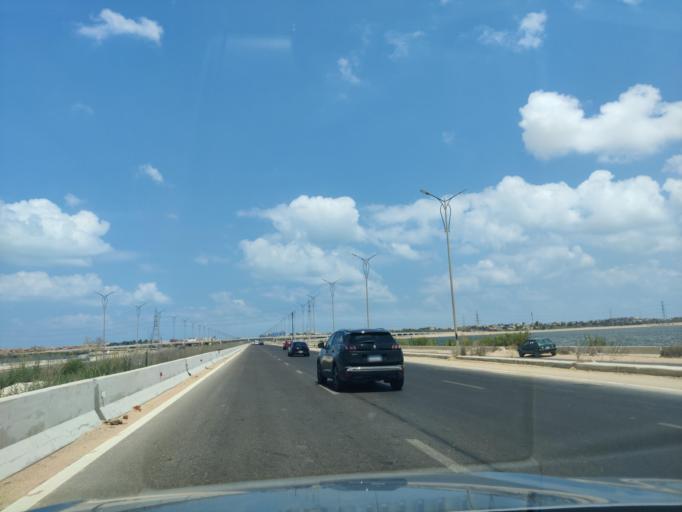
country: EG
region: Alexandria
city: Alexandria
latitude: 30.9966
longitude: 29.6464
